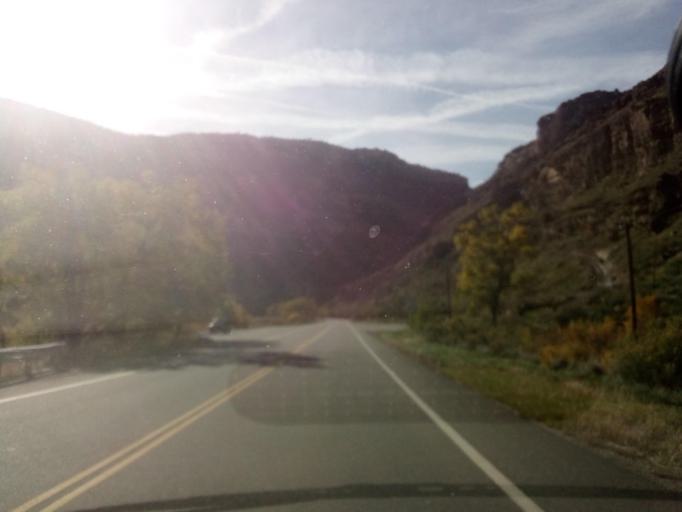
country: US
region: Colorado
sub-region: Mesa County
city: Palisade
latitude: 39.1812
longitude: -108.2788
